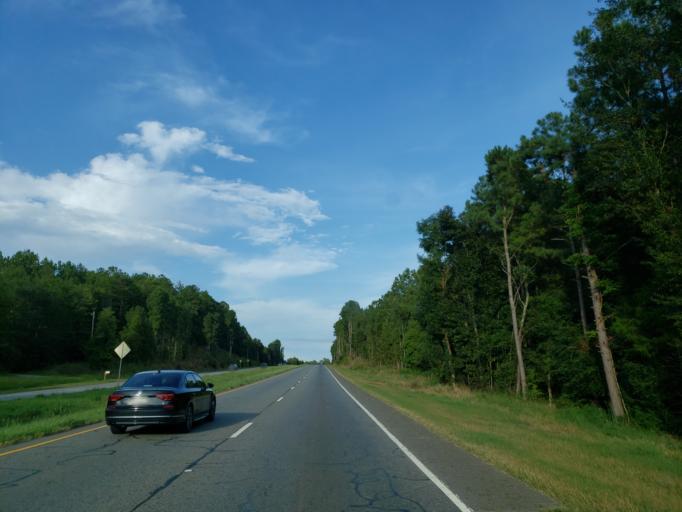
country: US
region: Georgia
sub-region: Bartow County
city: Euharlee
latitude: 34.2094
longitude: -84.9767
